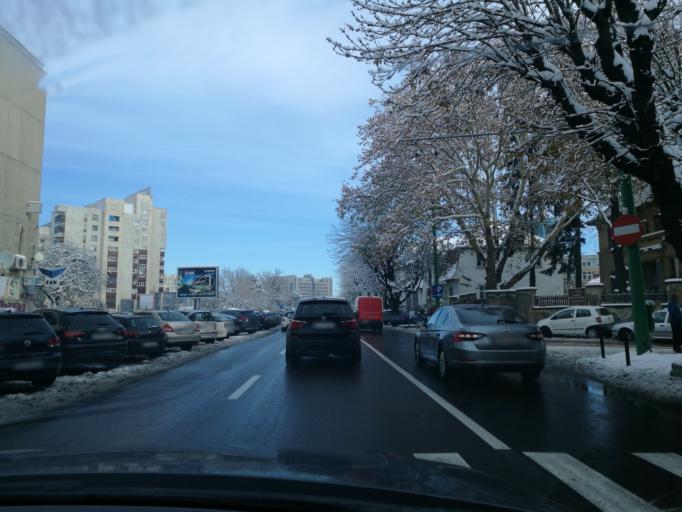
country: RO
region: Brasov
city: Brasov
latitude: 45.6498
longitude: 25.6070
